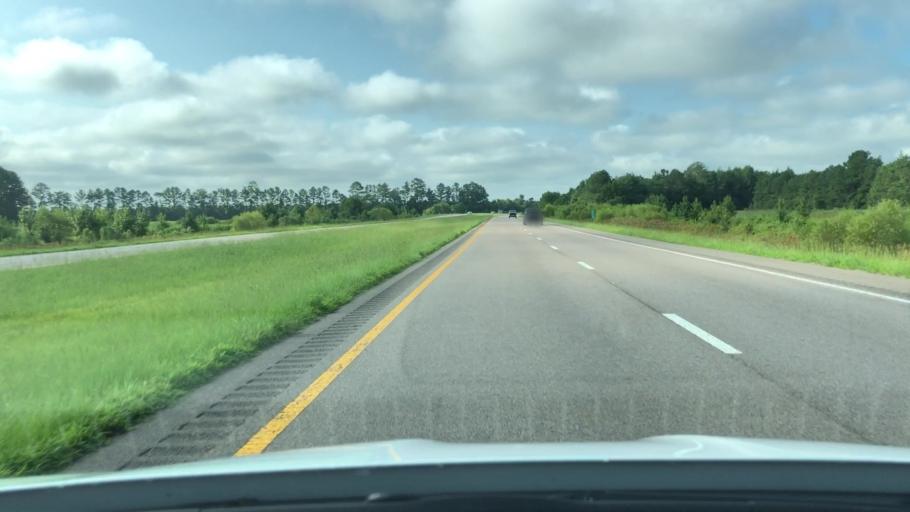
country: US
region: Virginia
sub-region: City of Portsmouth
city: Portsmouth Heights
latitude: 36.6829
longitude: -76.3474
